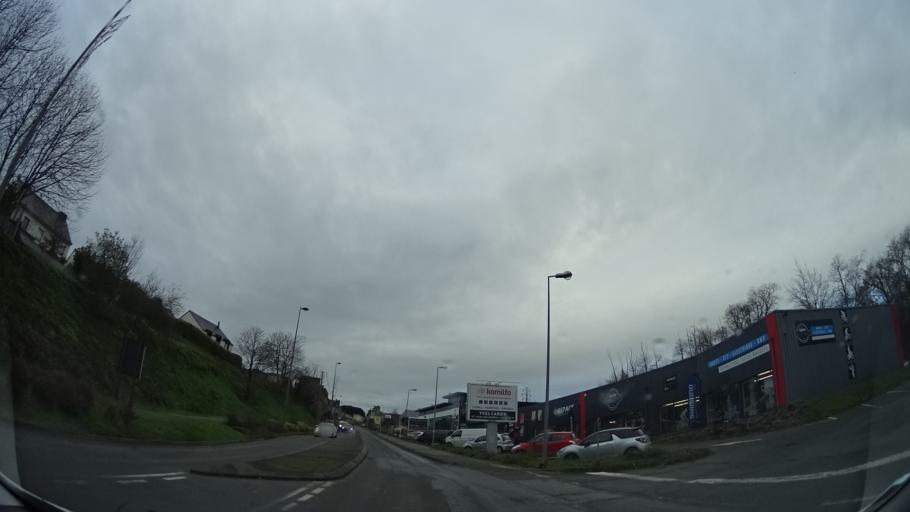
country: FR
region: Brittany
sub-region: Departement des Cotes-d'Armor
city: Lehon
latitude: 48.4502
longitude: -2.0683
